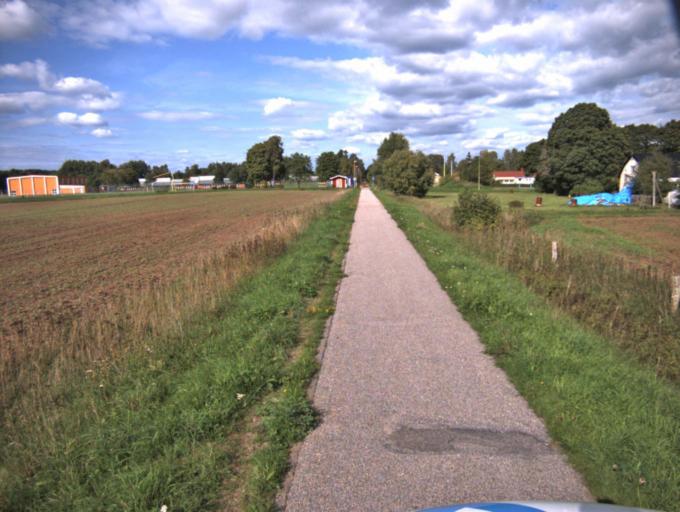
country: SE
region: Vaestra Goetaland
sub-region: Ulricehamns Kommun
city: Ulricehamn
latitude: 57.8541
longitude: 13.4276
